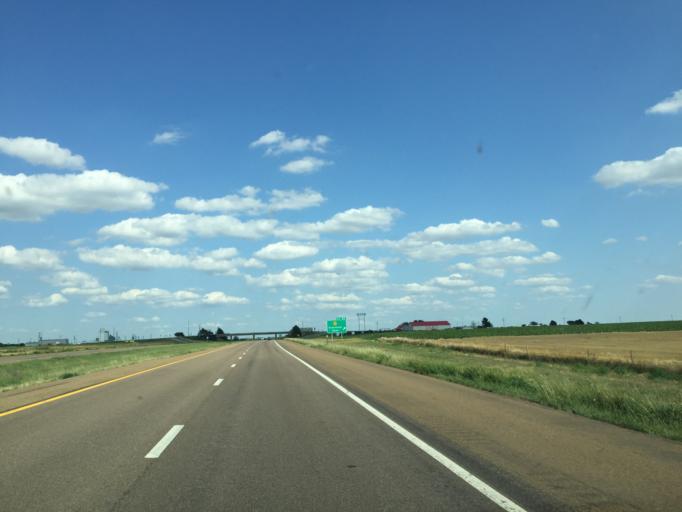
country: US
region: Kansas
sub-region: Gove County
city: Gove
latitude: 39.1107
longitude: -100.4858
